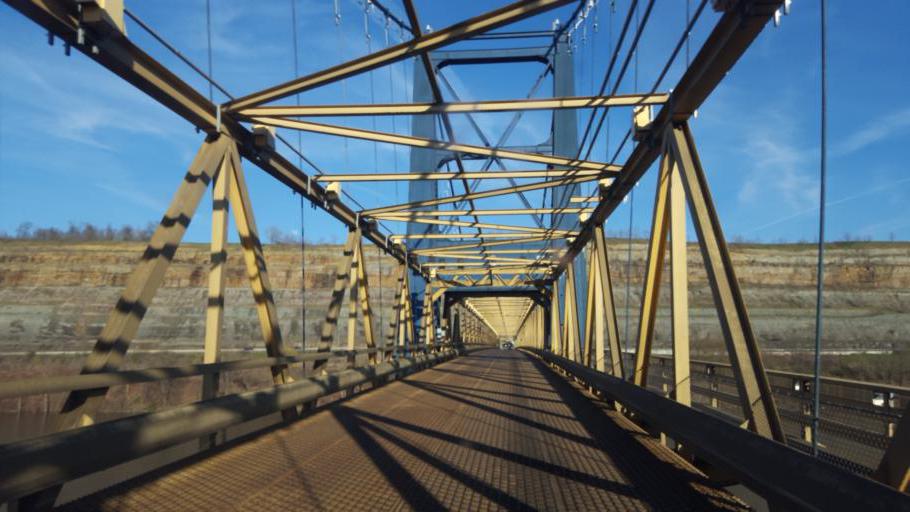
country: US
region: Ohio
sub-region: Jefferson County
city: Steubenville
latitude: 40.3585
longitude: -80.6104
